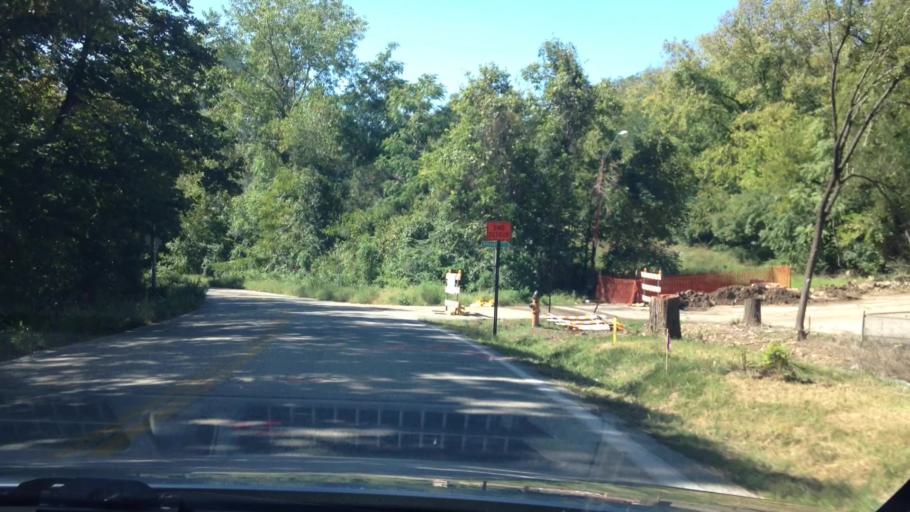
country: US
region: Missouri
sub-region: Jackson County
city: Raytown
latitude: 39.0038
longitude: -94.5096
